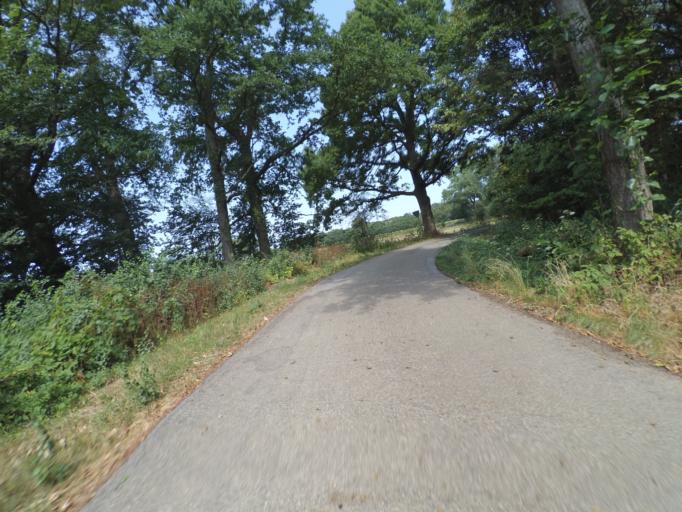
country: DE
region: North Rhine-Westphalia
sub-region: Regierungsbezirk Dusseldorf
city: Mehrhoog
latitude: 51.7581
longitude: 6.4738
